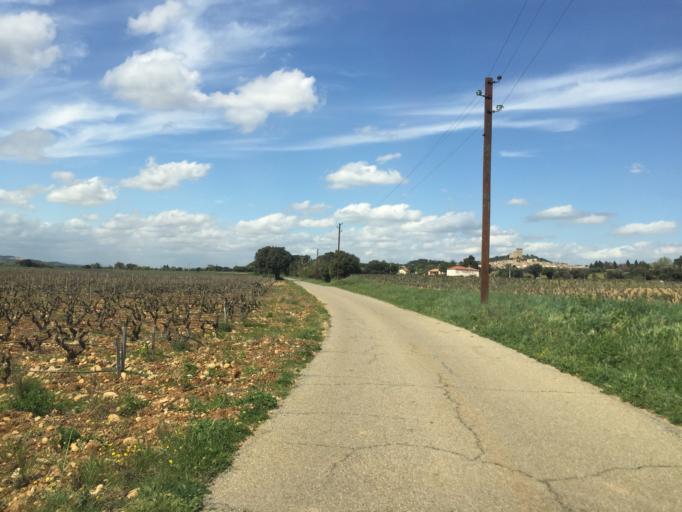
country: FR
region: Provence-Alpes-Cote d'Azur
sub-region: Departement du Vaucluse
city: Chateauneuf-du-Pape
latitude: 44.0454
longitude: 4.8429
